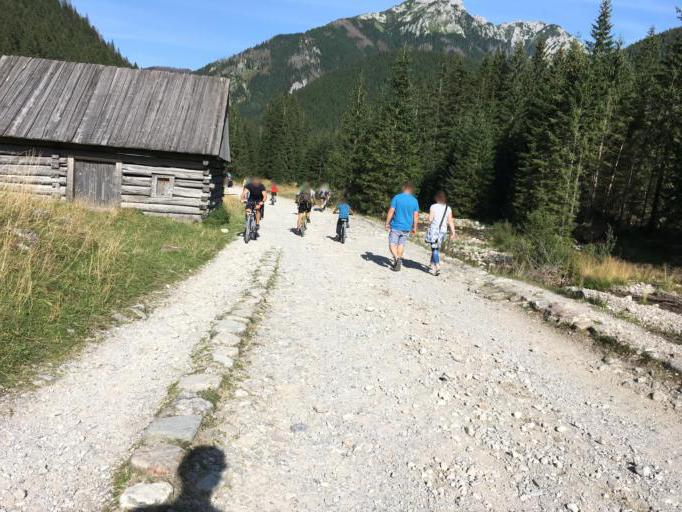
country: PL
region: Lesser Poland Voivodeship
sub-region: Powiat tatrzanski
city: Koscielisko
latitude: 49.2373
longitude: 19.7964
